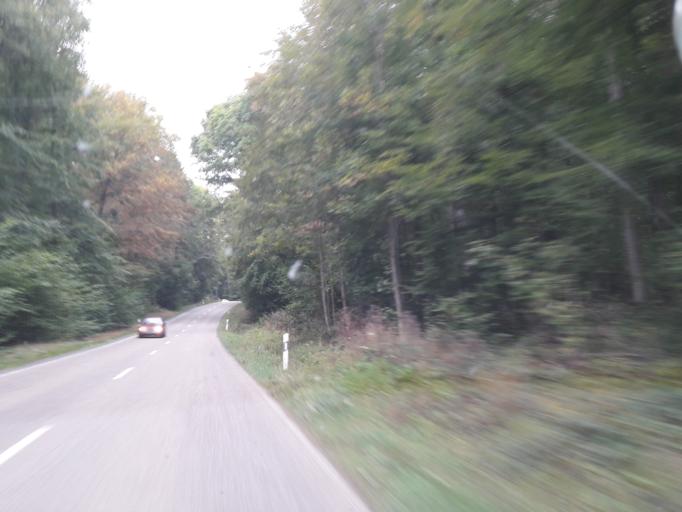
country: DE
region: Baden-Wuerttemberg
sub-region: Regierungsbezirk Stuttgart
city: Widdern
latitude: 49.2989
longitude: 9.3964
